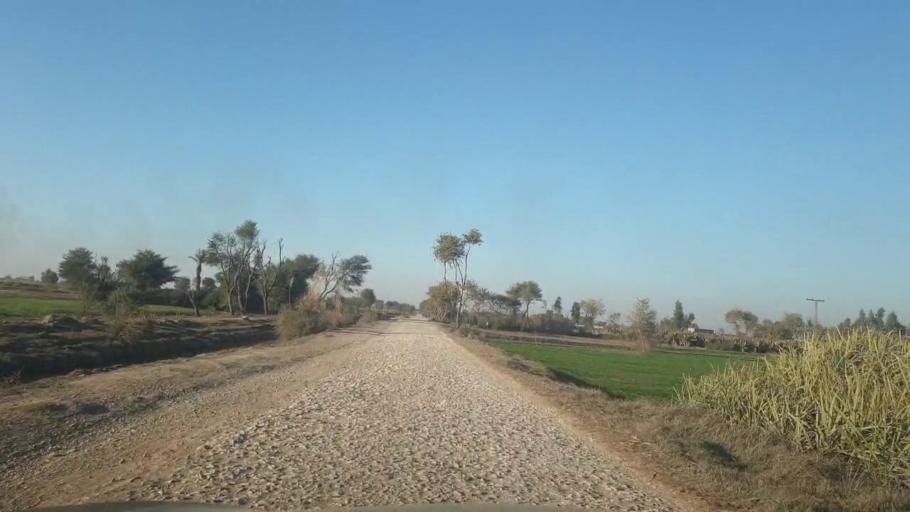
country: PK
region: Sindh
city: Ghotki
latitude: 27.9986
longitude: 69.2712
